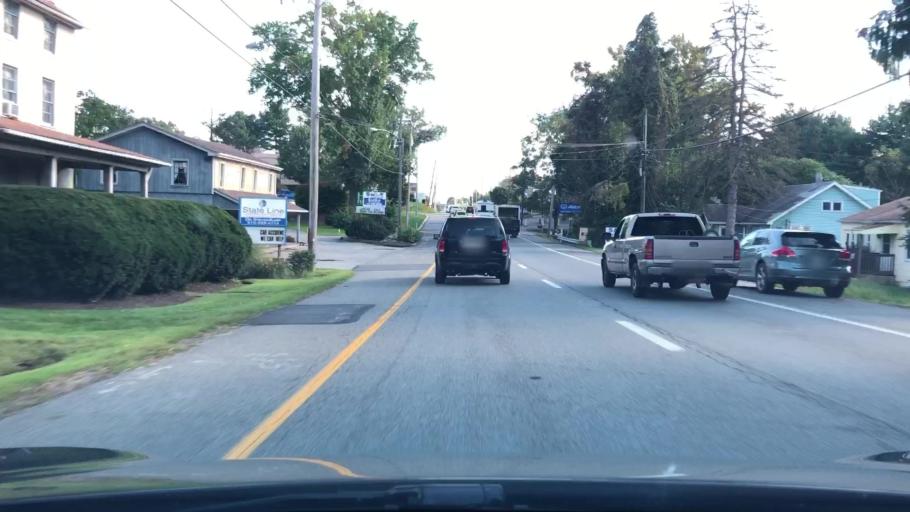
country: US
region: Pennsylvania
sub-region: Delaware County
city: Chester Heights
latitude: 39.8548
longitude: -75.5412
